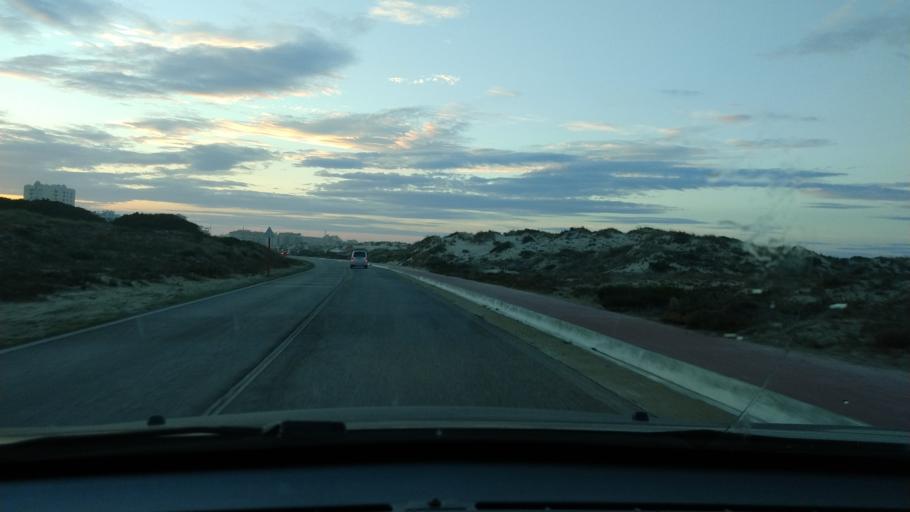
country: PT
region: Leiria
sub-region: Peniche
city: Peniche
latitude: 39.3583
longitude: -9.3599
